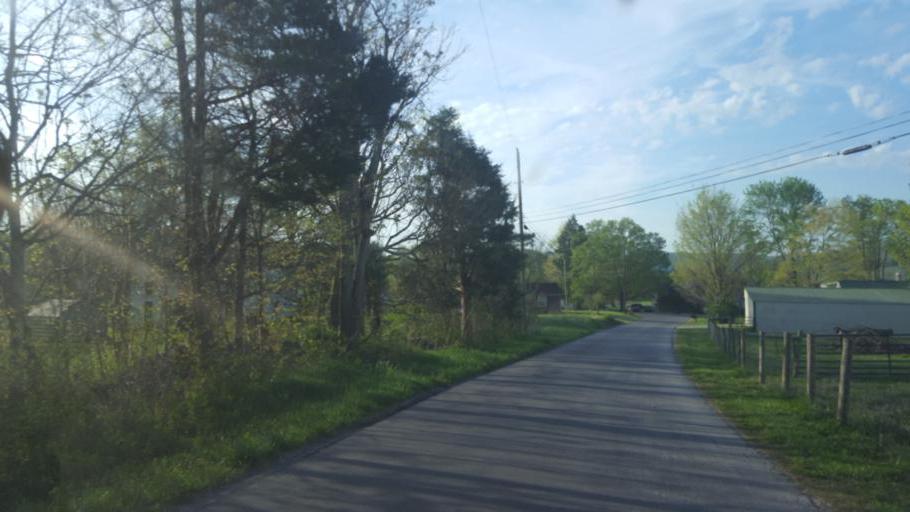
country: US
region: Kentucky
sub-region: Hart County
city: Munfordville
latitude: 37.2418
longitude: -85.8950
